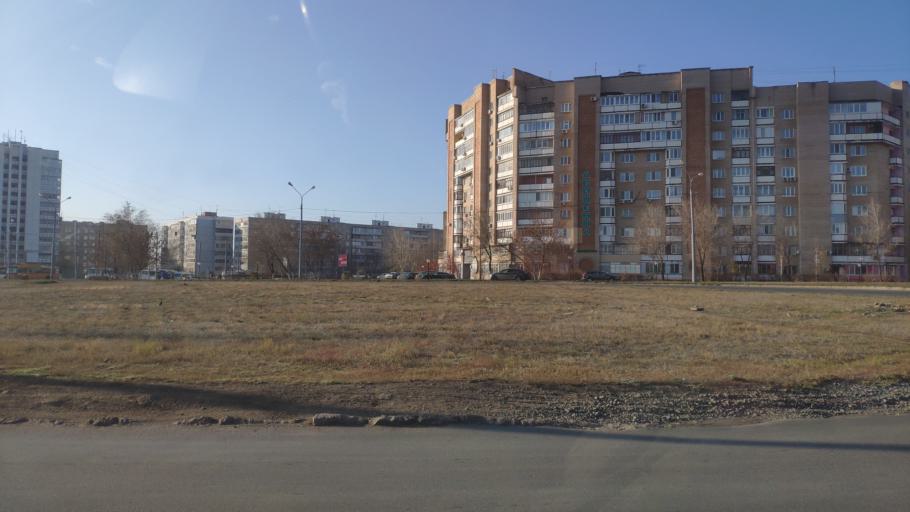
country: RU
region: Orenburg
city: Prigorodnyy
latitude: 51.7755
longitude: 55.1930
